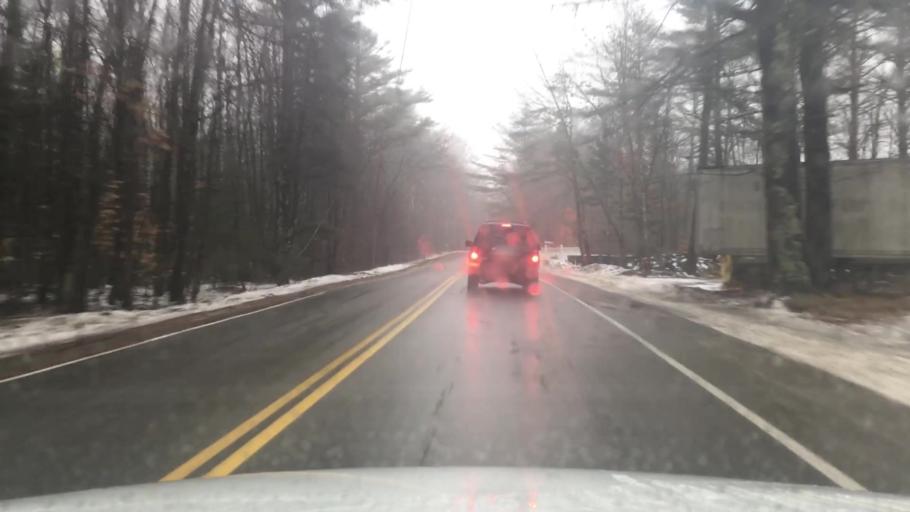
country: US
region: Maine
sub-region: Cumberland County
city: Westbrook
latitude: 43.6354
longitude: -70.3762
